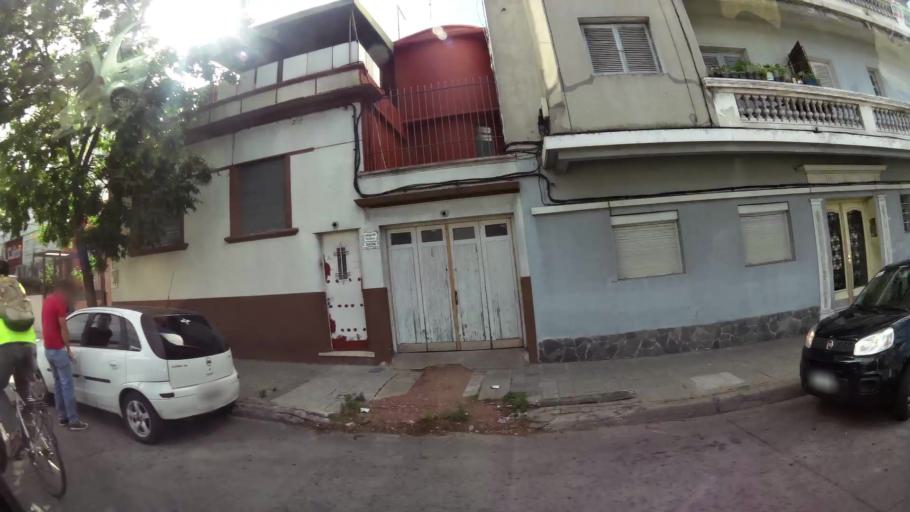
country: UY
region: Montevideo
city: Montevideo
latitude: -34.8837
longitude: -56.1612
